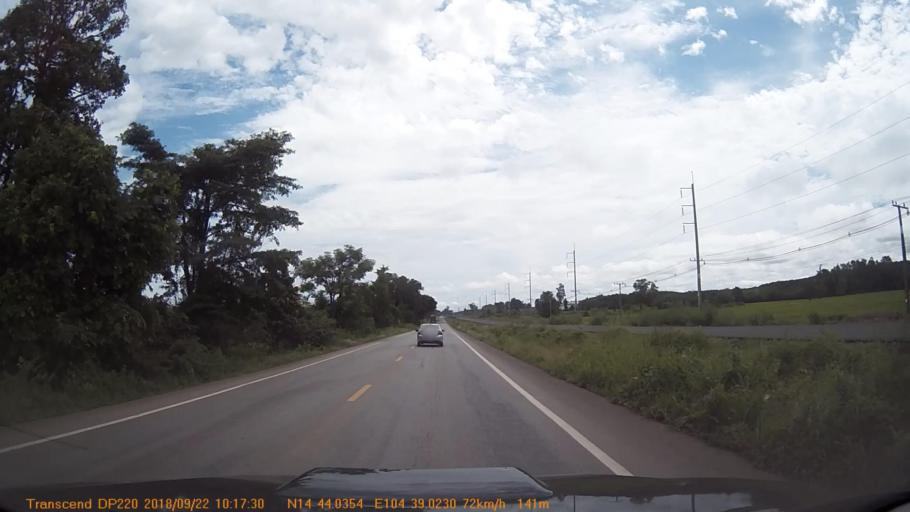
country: TH
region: Sisaket
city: Benchalak
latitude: 14.7339
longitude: 104.6503
